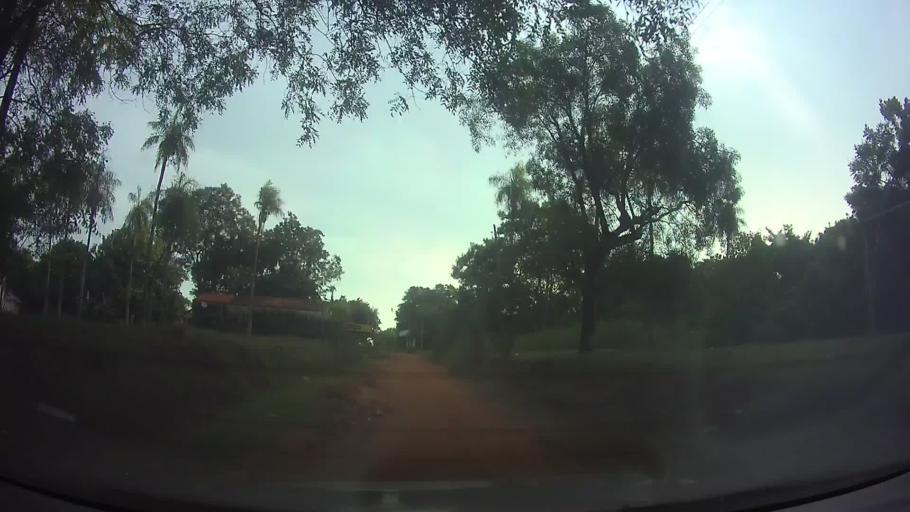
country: PY
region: Central
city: Limpio
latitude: -25.2430
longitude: -57.4489
